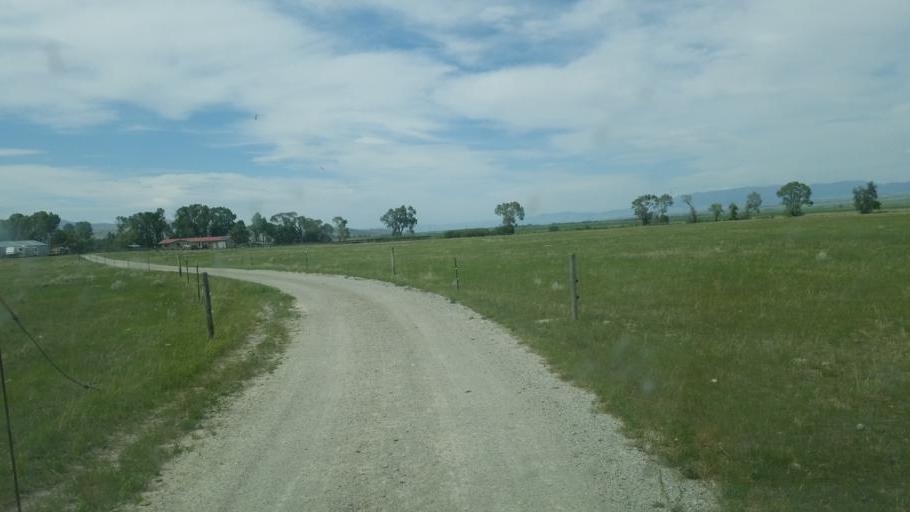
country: US
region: Montana
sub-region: Broadwater County
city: Townsend
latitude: 46.1859
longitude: -111.4809
